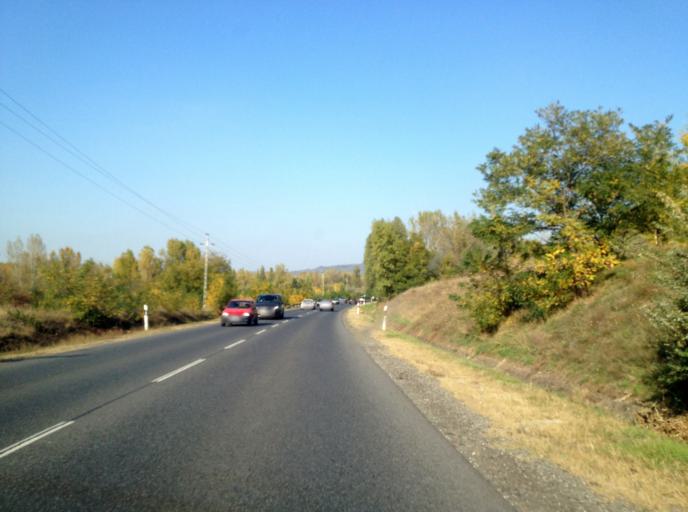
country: HU
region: Komarom-Esztergom
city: Dorog
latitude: 47.7520
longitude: 18.7385
